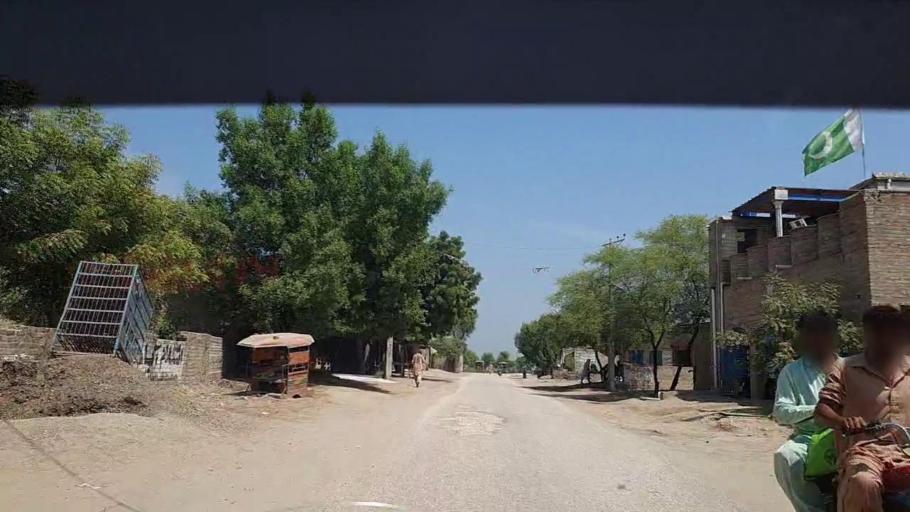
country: PK
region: Sindh
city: Rustam jo Goth
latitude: 28.0842
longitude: 68.7877
